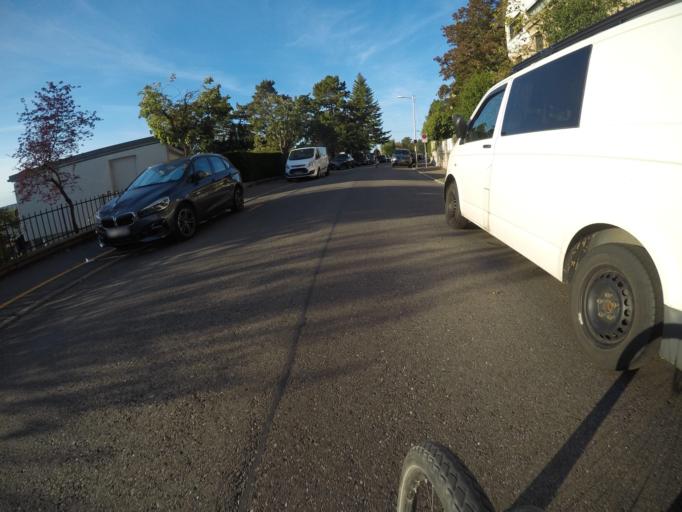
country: DE
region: Baden-Wuerttemberg
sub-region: Regierungsbezirk Stuttgart
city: Stuttgart
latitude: 48.7713
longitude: 9.1892
